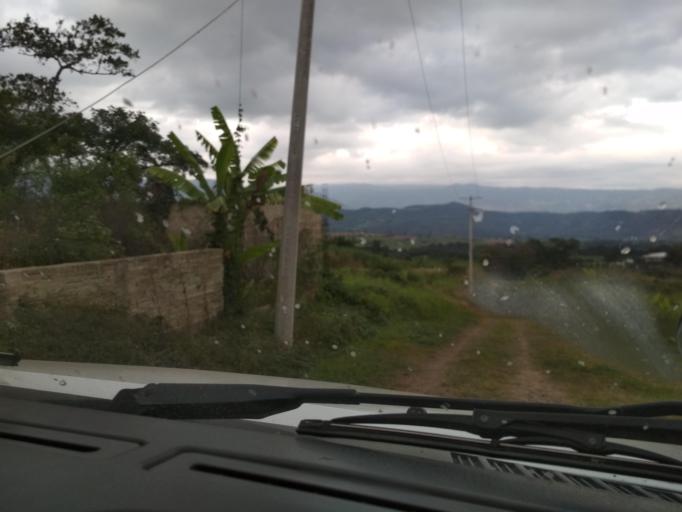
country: MX
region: Veracruz
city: El Castillo
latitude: 19.5703
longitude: -96.8312
